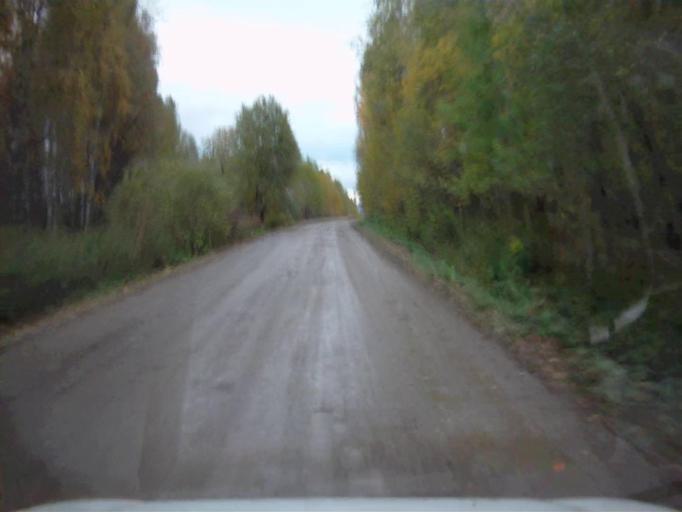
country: RU
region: Sverdlovsk
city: Mikhaylovsk
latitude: 56.1932
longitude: 59.1945
